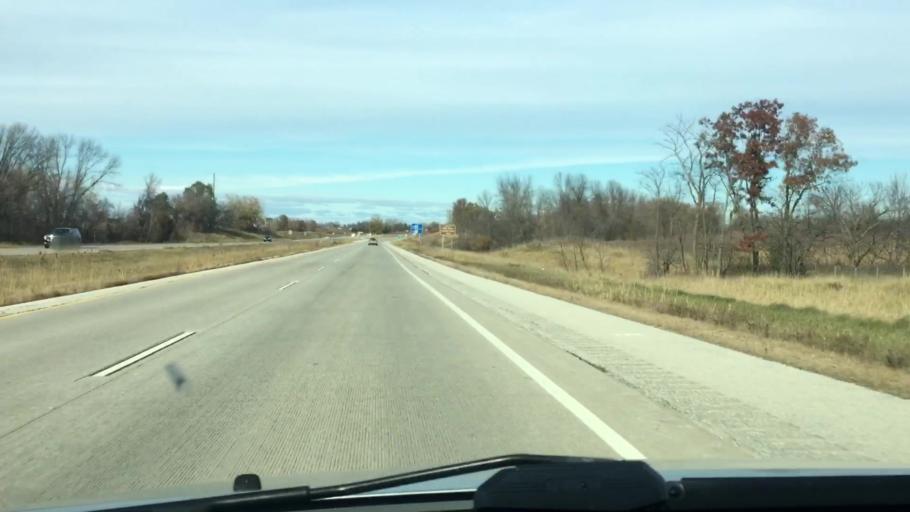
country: US
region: Wisconsin
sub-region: Kewaunee County
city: Luxemburg
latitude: 44.6424
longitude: -87.7535
